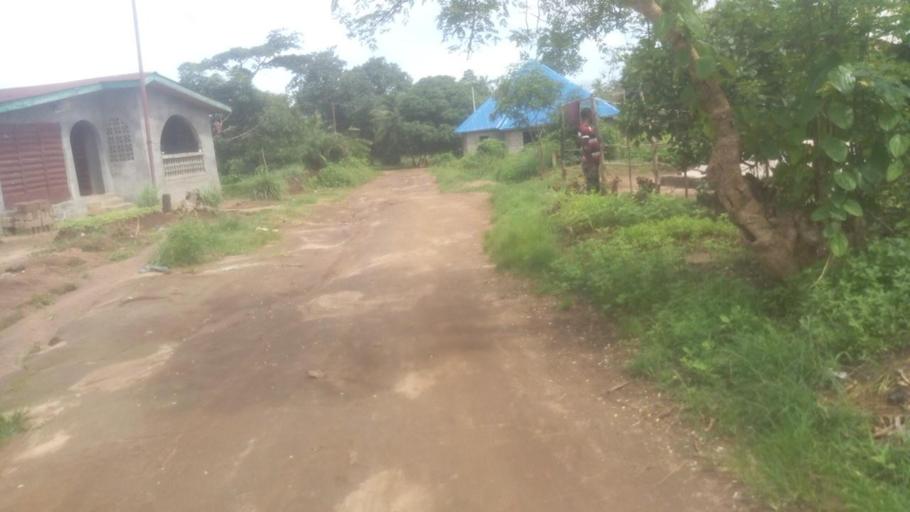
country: SL
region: Northern Province
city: Masoyila
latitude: 8.5946
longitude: -13.1952
